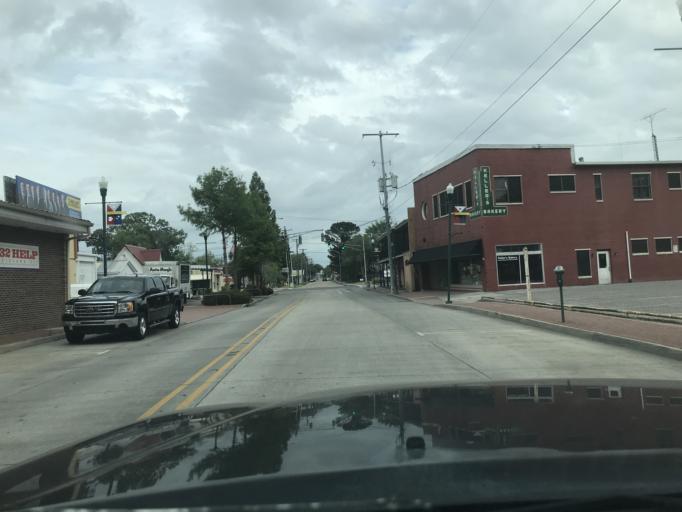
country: US
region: Louisiana
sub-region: Lafayette Parish
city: Lafayette
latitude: 30.2206
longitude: -92.0179
